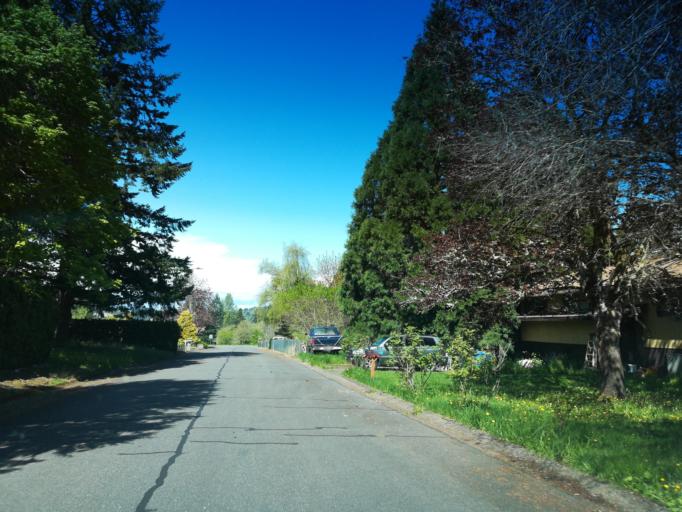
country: US
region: Oregon
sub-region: Clackamas County
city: Damascus
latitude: 45.4311
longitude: -122.4307
